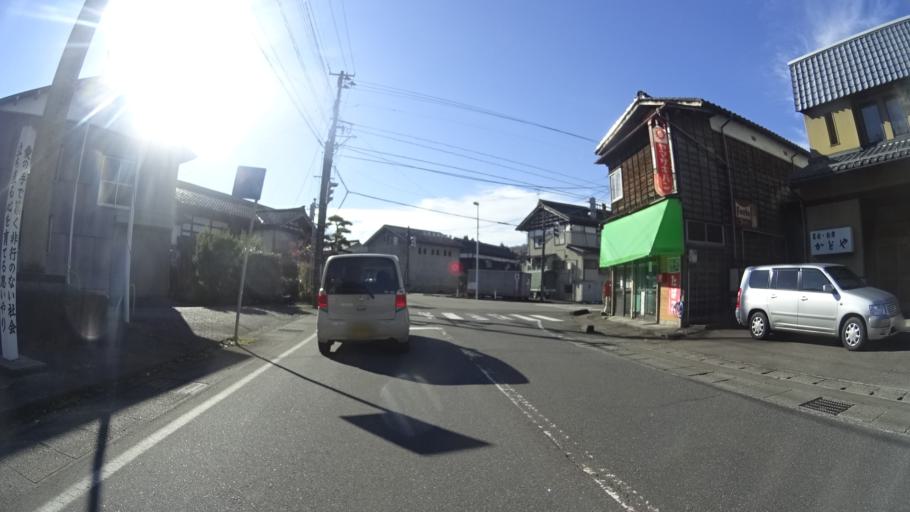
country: JP
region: Niigata
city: Tochio-honcho
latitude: 37.4907
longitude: 138.9742
